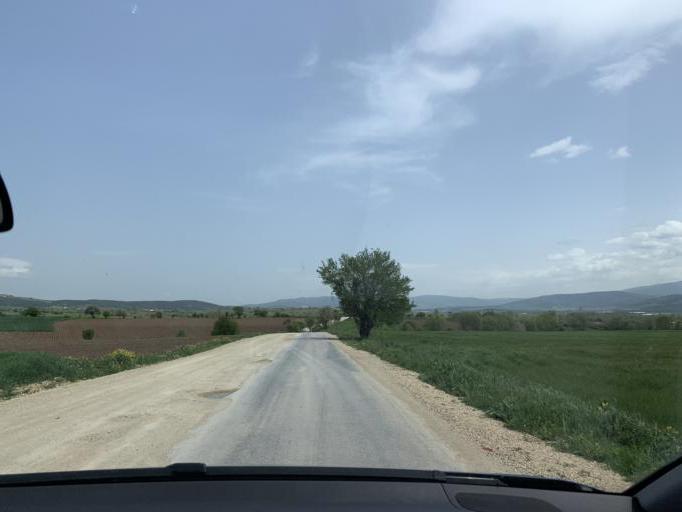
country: TR
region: Bolu
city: Bolu
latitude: 40.7574
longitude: 31.6810
